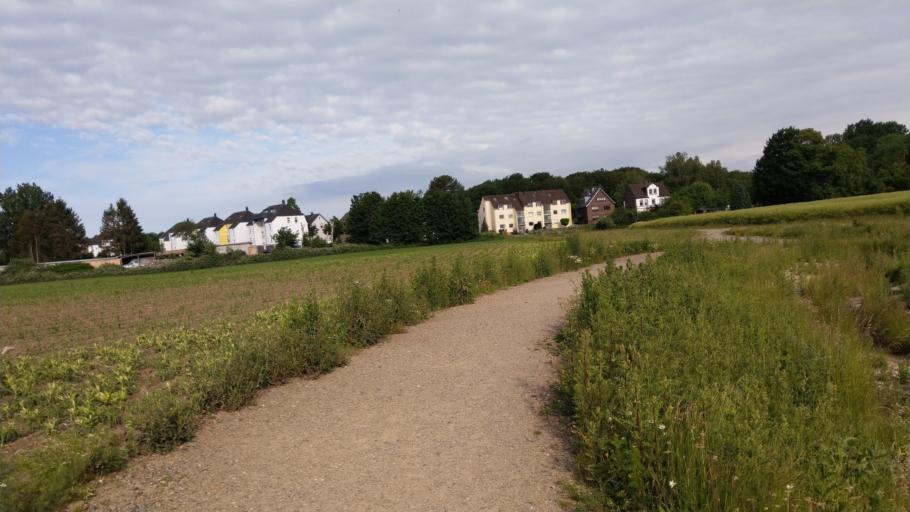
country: DE
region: North Rhine-Westphalia
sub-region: Regierungsbezirk Arnsberg
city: Herne
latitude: 51.5822
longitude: 7.2549
